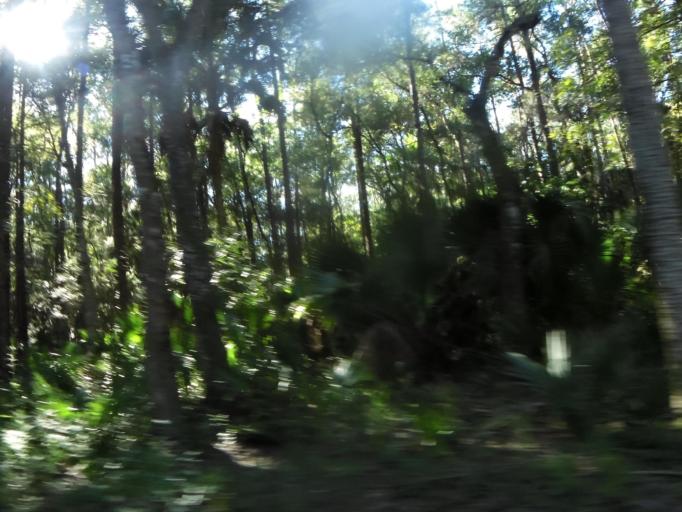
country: US
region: Florida
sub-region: Duval County
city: Atlantic Beach
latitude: 30.4215
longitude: -81.4345
